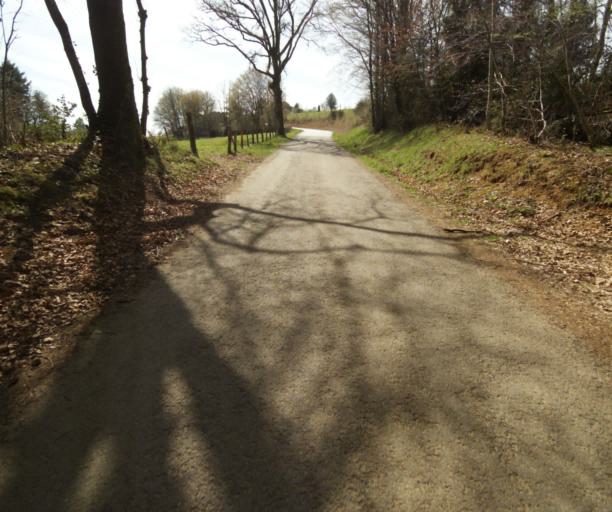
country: FR
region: Limousin
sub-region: Departement de la Correze
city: Naves
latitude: 45.3619
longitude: 1.7977
